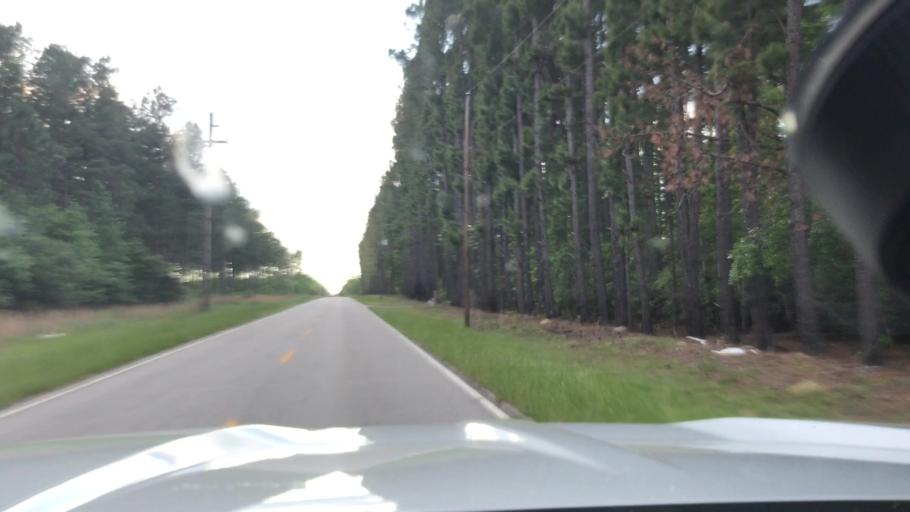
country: US
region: South Carolina
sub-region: Bamberg County
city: Denmark
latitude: 33.4601
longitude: -81.1497
